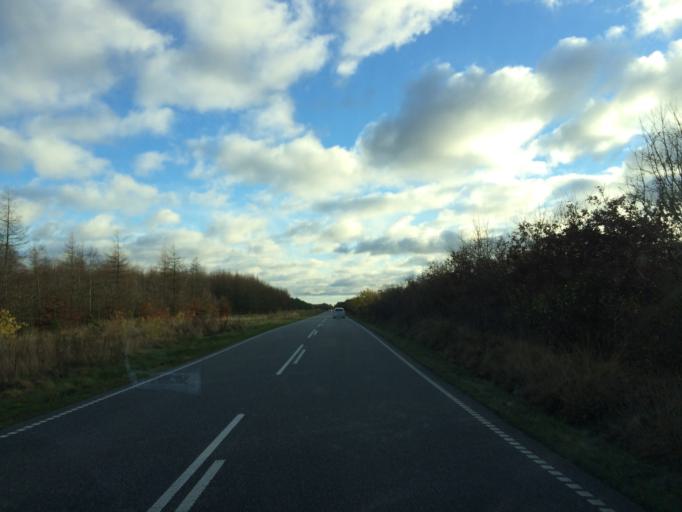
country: DK
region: Central Jutland
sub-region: Herning Kommune
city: Kibaek
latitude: 55.9460
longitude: 8.8858
